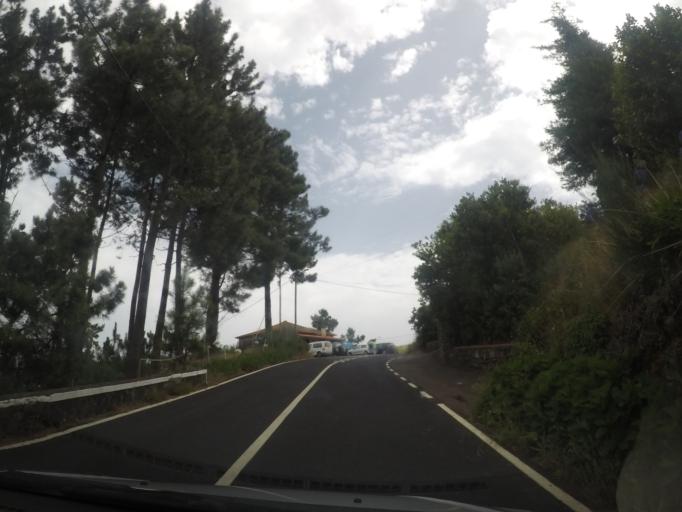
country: PT
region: Madeira
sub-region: Santa Cruz
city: Camacha
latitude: 32.6900
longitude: -16.8424
